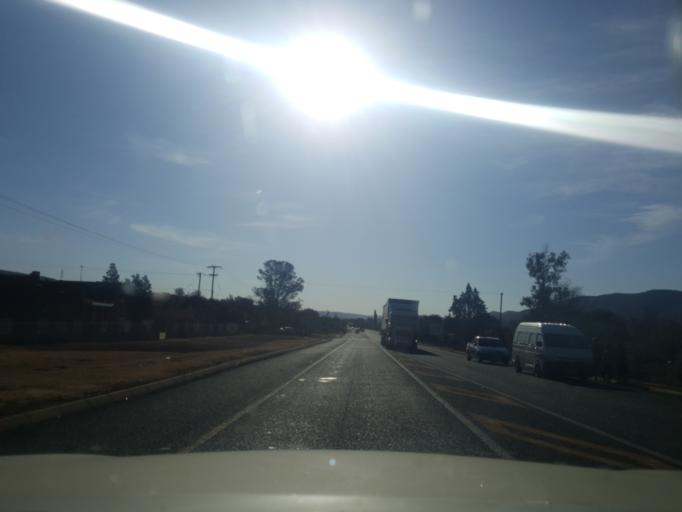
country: ZA
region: North-West
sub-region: Ngaka Modiri Molema District Municipality
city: Zeerust
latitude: -25.4502
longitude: 25.8677
